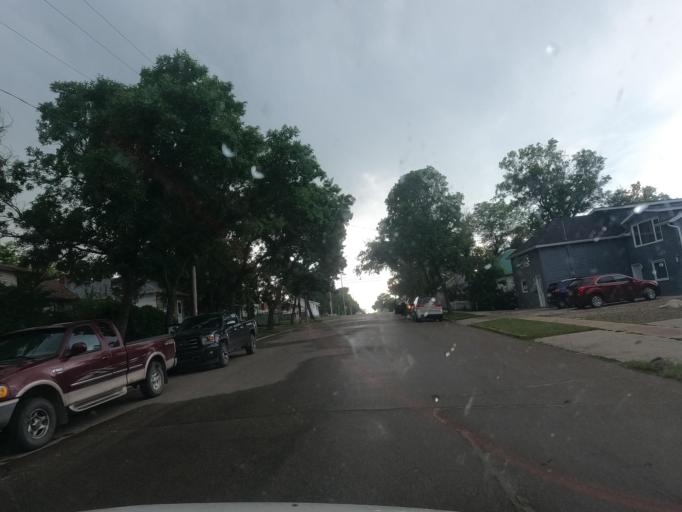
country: CA
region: Saskatchewan
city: Weyburn
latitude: 49.6574
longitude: -103.8530
